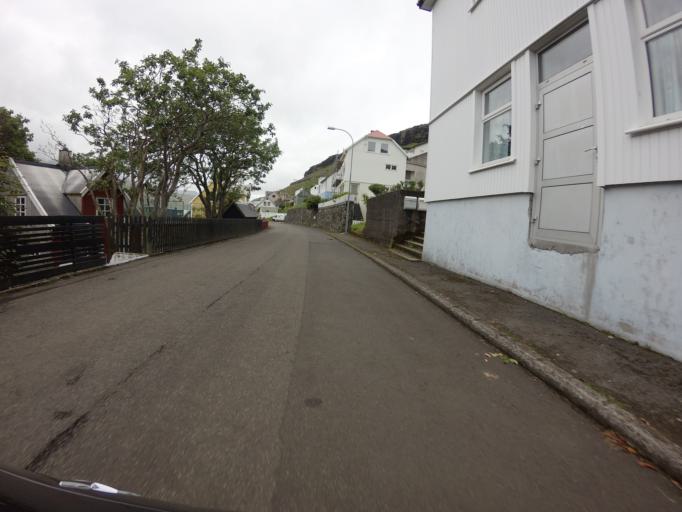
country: FO
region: Eysturoy
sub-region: Eidi
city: Eidi
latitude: 62.2746
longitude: -7.0936
